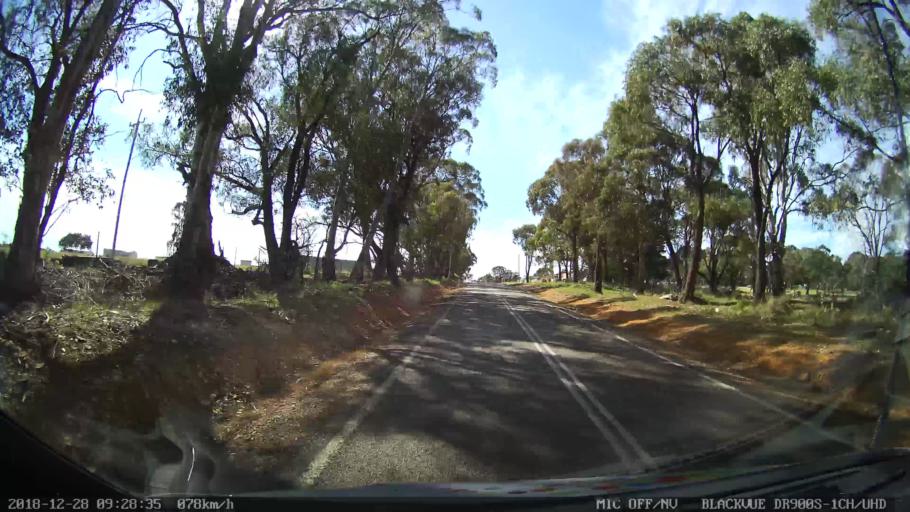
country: AU
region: New South Wales
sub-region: Upper Lachlan Shire
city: Crookwell
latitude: -34.4401
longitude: 149.4177
